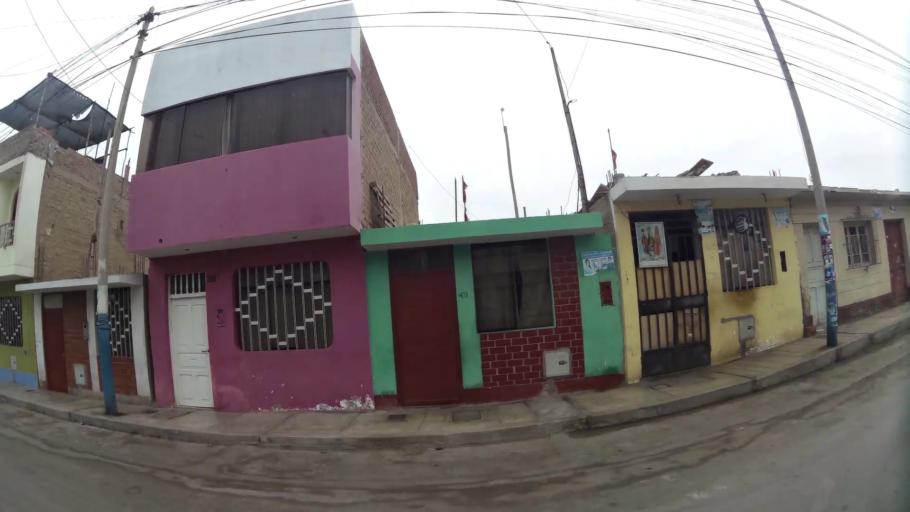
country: PE
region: Ica
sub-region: Provincia de Pisco
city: Pisco
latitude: -13.7308
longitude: -76.2213
